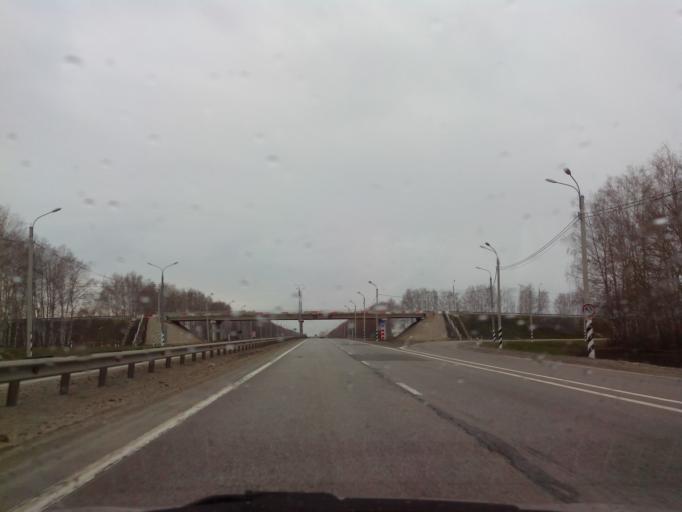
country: RU
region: Tambov
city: Selezni
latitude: 52.7596
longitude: 41.1377
